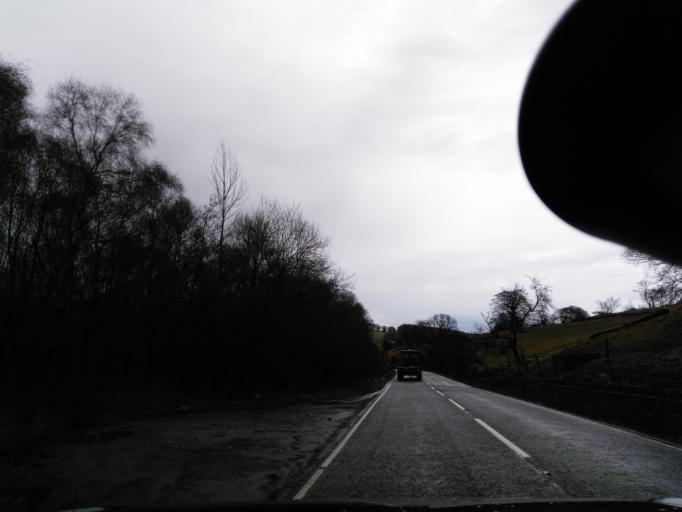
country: GB
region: England
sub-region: Bradford
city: Burley in Wharfedale
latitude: 53.9928
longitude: -1.7522
